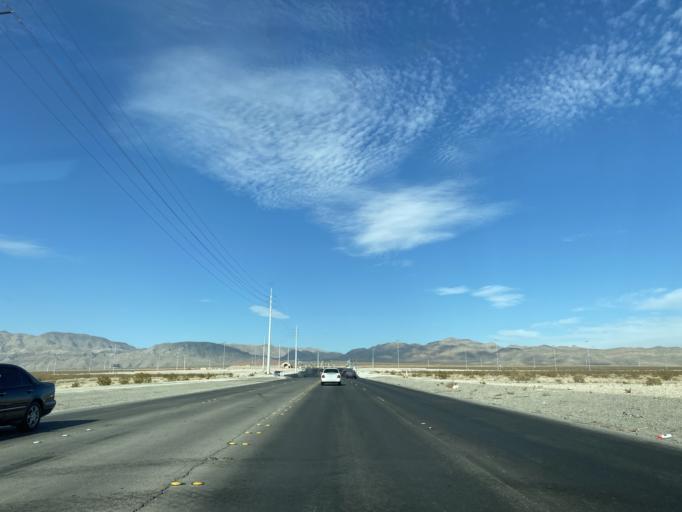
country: US
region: Nevada
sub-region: Clark County
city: Nellis Air Force Base
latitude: 36.2843
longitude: -115.0798
